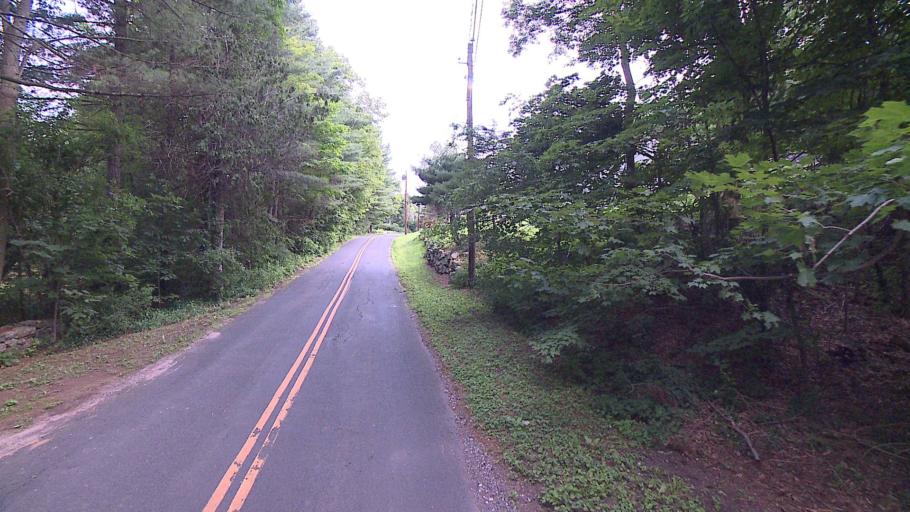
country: US
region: Connecticut
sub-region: Litchfield County
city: Winsted
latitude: 41.9590
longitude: -73.0163
